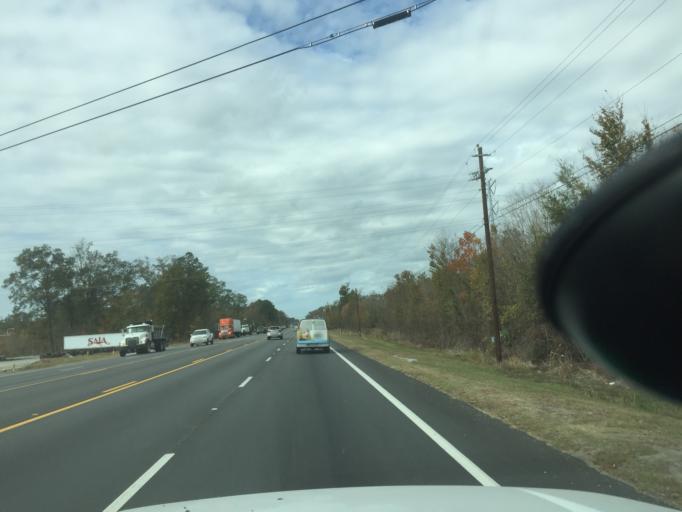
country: US
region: Georgia
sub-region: Chatham County
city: Garden City
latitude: 32.0900
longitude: -81.1844
